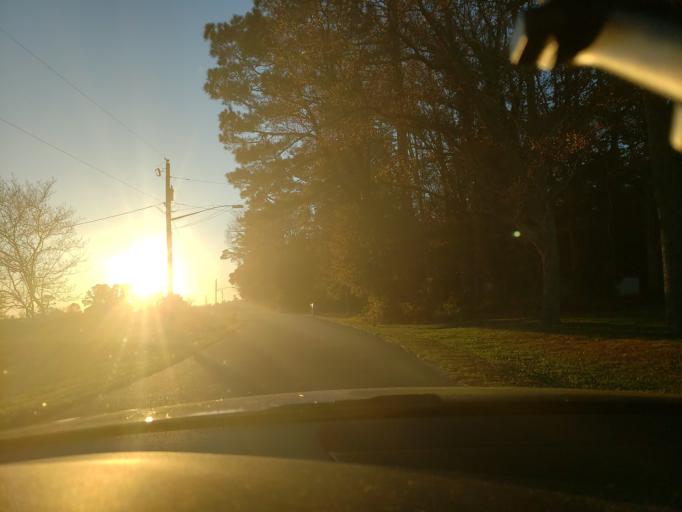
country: US
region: Virginia
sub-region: City of Chesapeake
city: Chesapeake
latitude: 36.7045
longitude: -76.1574
